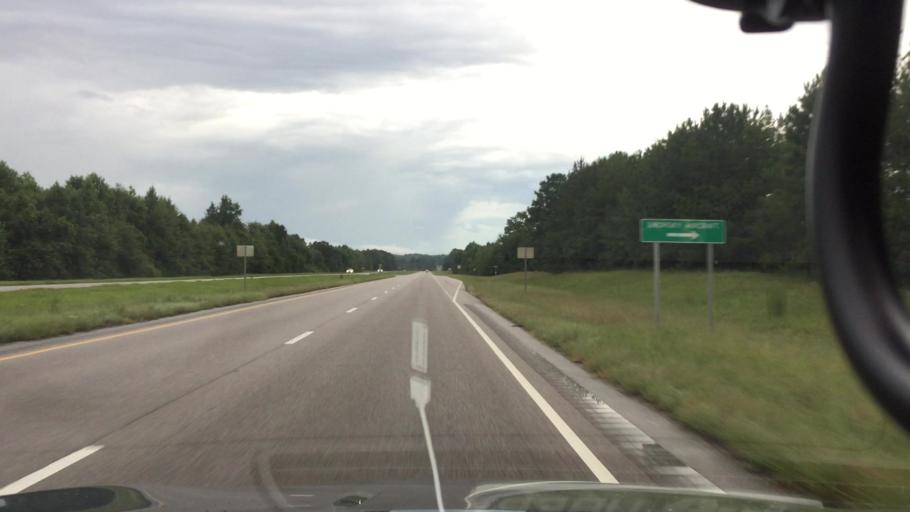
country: US
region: Alabama
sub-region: Pike County
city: Troy
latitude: 31.8645
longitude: -85.9994
